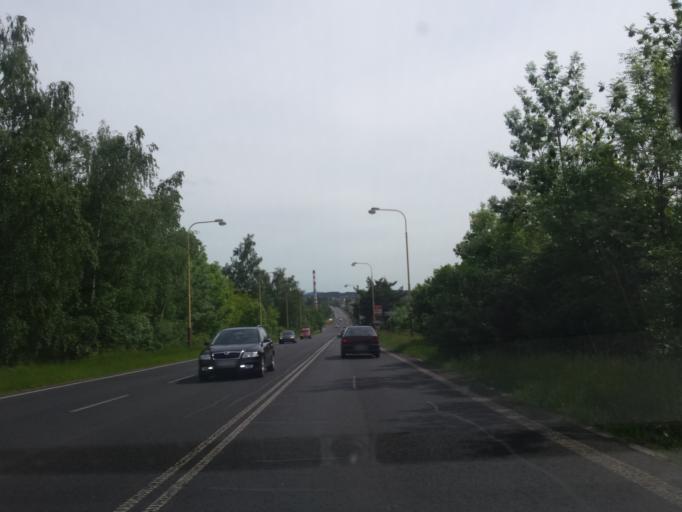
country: CZ
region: Liberecky
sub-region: Okres Ceska Lipa
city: Ceska Lipa
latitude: 50.6879
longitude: 14.5415
